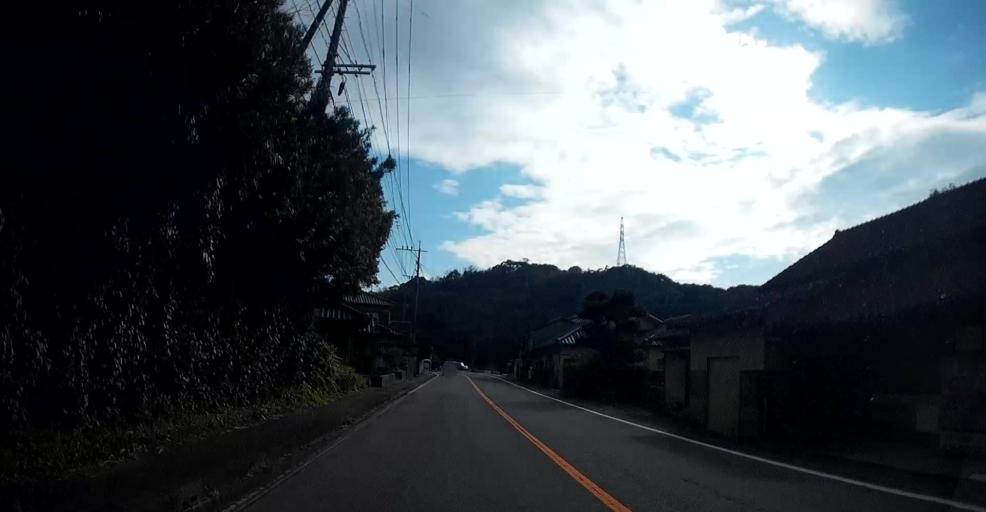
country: JP
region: Kumamoto
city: Yatsushiro
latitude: 32.6141
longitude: 130.4620
